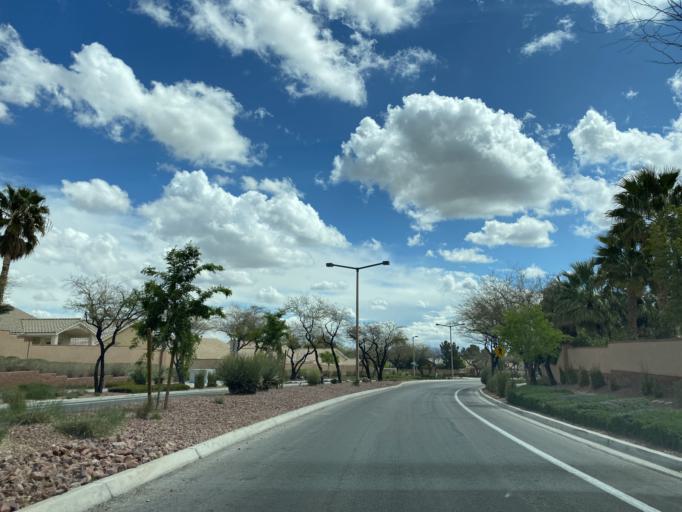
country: US
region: Nevada
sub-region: Clark County
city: Summerlin South
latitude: 36.1900
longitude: -115.3319
